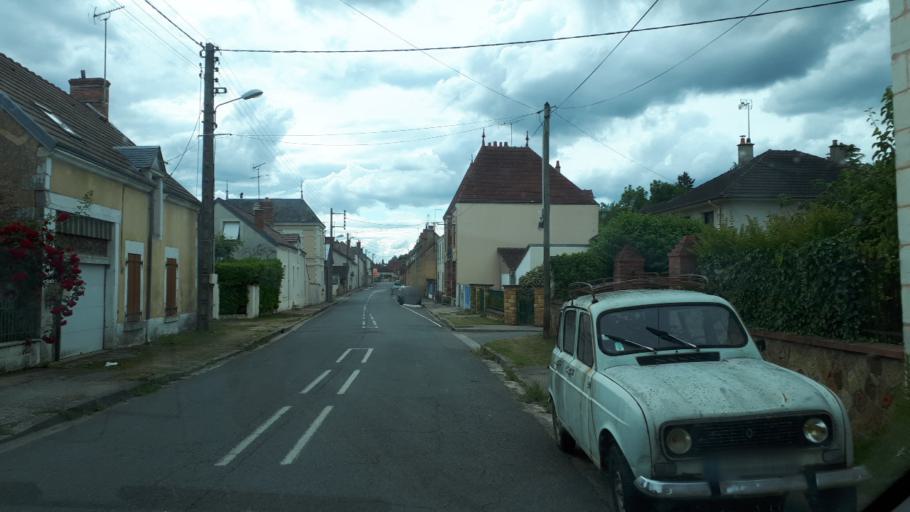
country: FR
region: Centre
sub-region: Departement du Cher
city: Gracay
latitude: 47.1432
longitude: 1.8514
